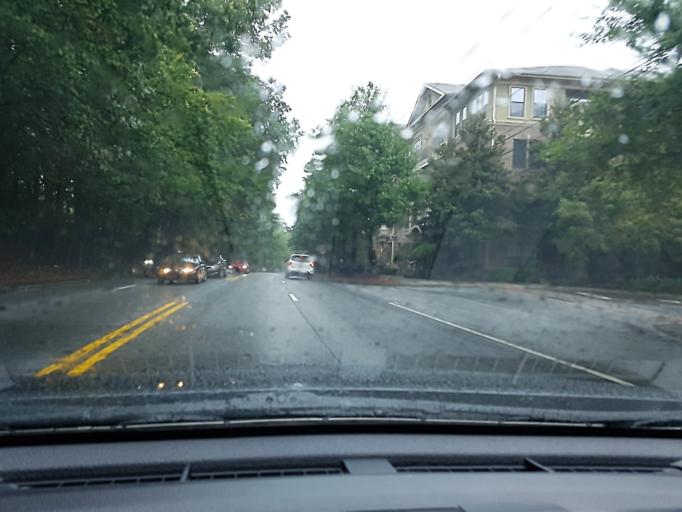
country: US
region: Georgia
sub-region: DeKalb County
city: North Atlanta
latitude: 33.8452
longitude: -84.3805
